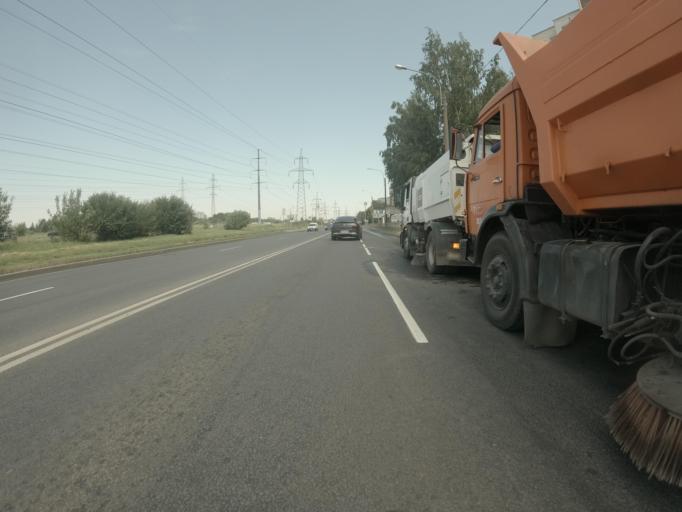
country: RU
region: St.-Petersburg
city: Krasnogvargeisky
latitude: 59.9477
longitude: 30.4610
